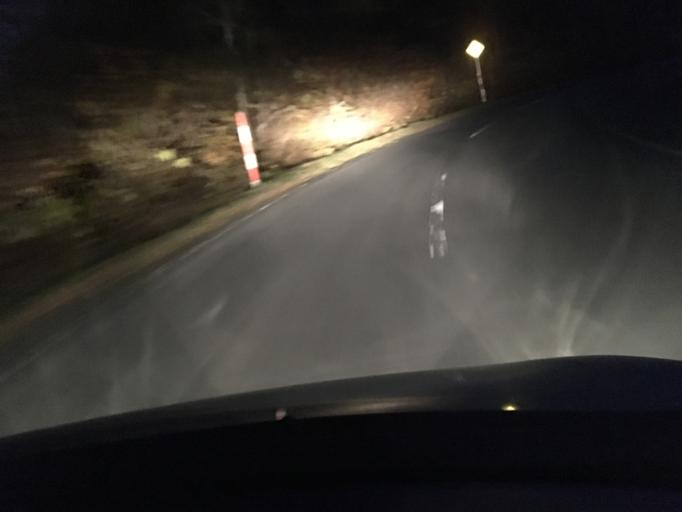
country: JP
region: Akita
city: Yuzawa
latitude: 38.9153
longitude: 140.7313
